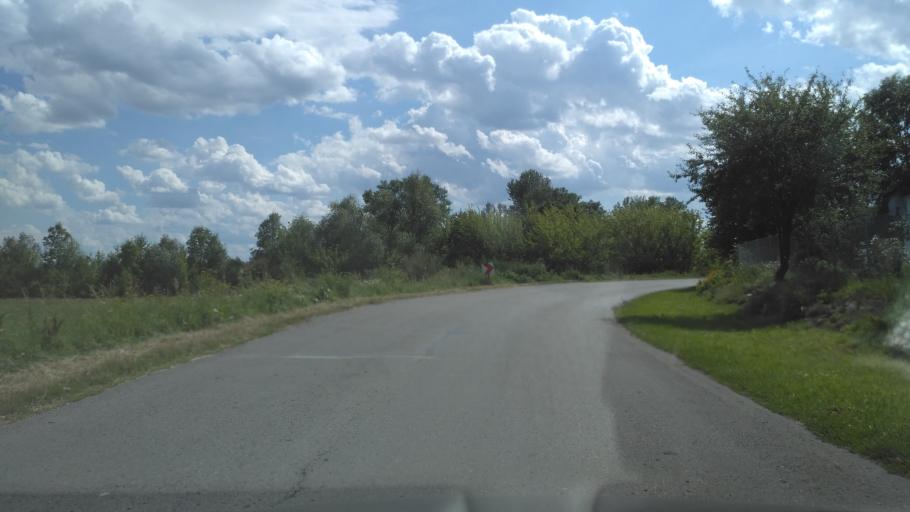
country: PL
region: Lublin Voivodeship
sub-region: Powiat leczynski
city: Milejow
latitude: 51.2148
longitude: 22.8895
